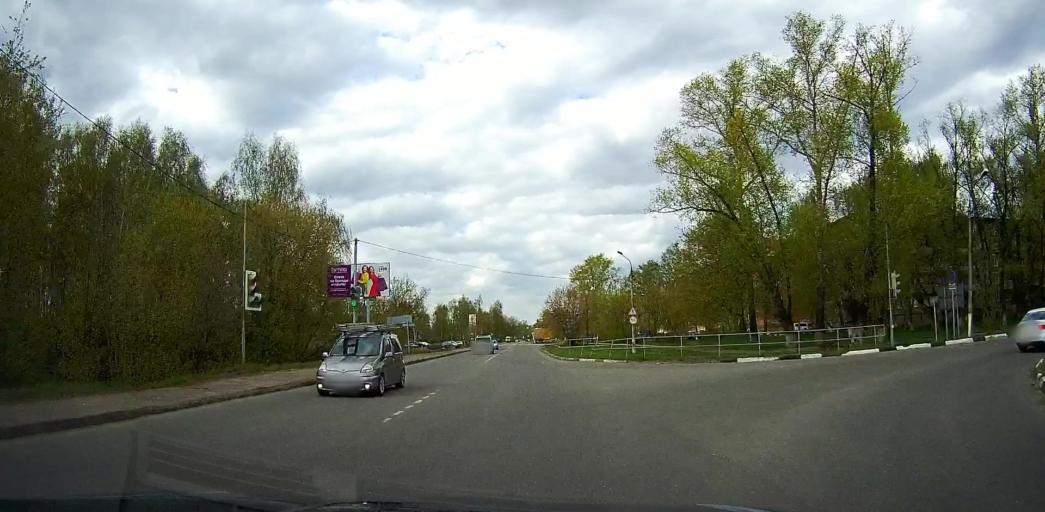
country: RU
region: Moskovskaya
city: Pavlovskiy Posad
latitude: 55.7652
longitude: 38.6564
